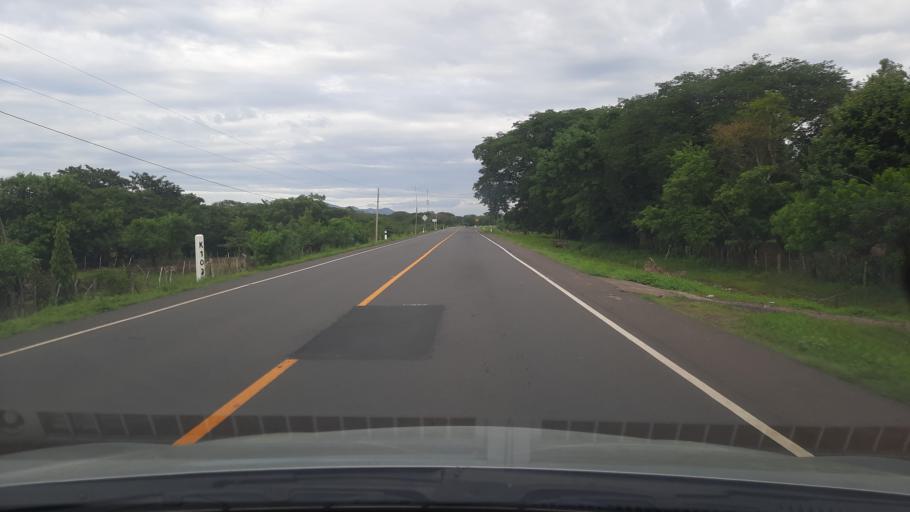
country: NI
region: Leon
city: Telica
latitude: 12.6513
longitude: -86.7505
